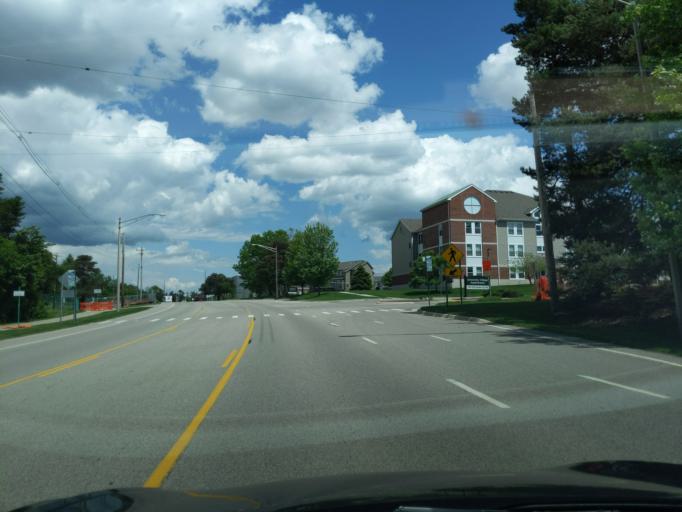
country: US
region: Michigan
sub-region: Ingham County
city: East Lansing
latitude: 42.7281
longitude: -84.4995
